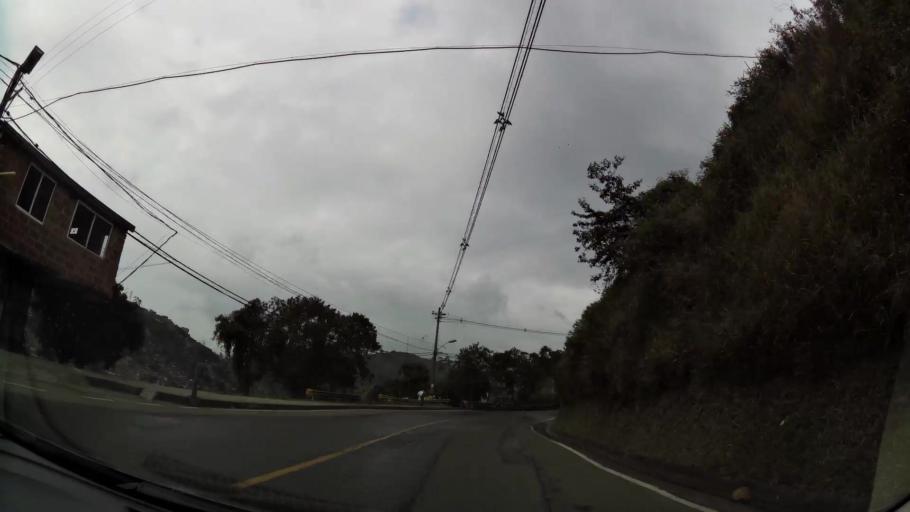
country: CO
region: Antioquia
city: Medellin
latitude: 6.2779
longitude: -75.6113
